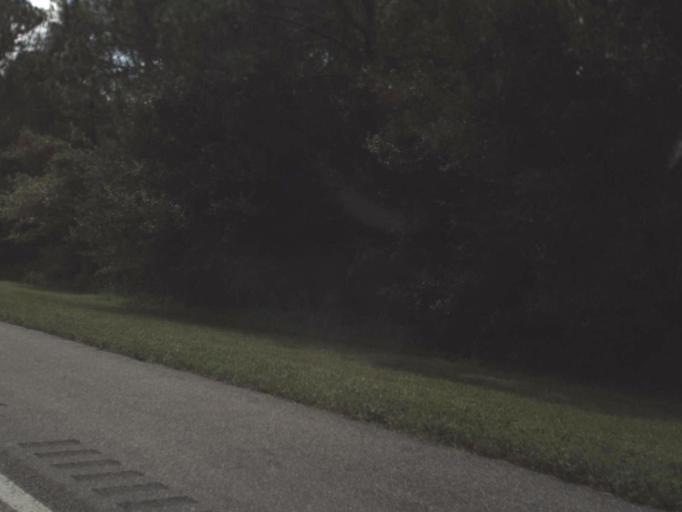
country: US
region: Florida
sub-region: Sarasota County
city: North Port
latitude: 27.0978
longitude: -82.1338
